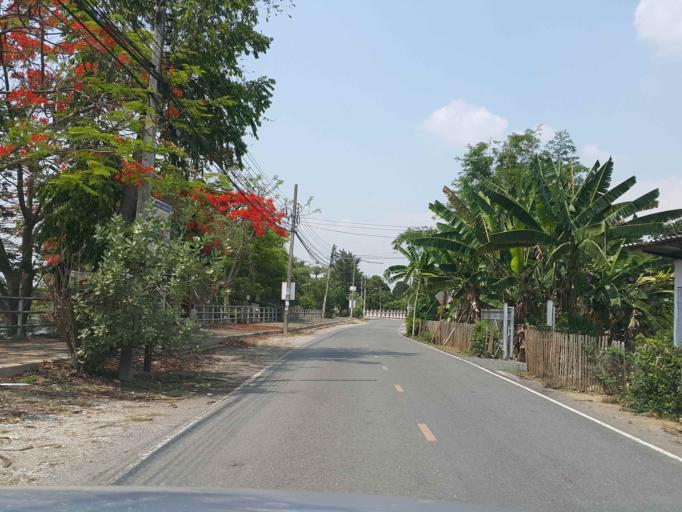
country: TH
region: Chiang Mai
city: Saraphi
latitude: 18.6965
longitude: 98.9866
